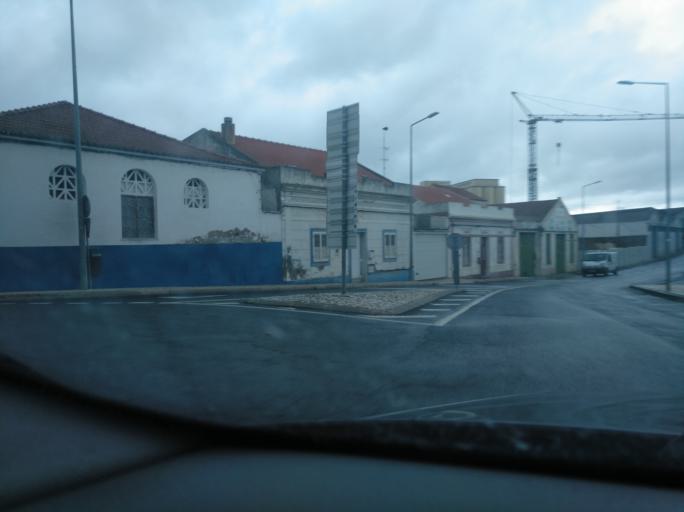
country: PT
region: Beja
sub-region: Aljustrel
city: Aljustrel
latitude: 37.8793
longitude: -8.1596
